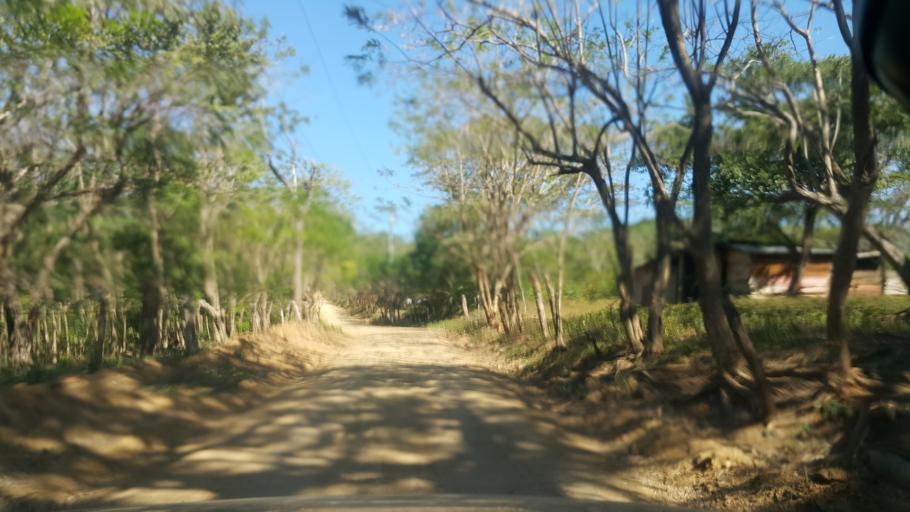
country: NI
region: Rivas
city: San Juan del Sur
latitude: 11.2830
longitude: -85.8798
